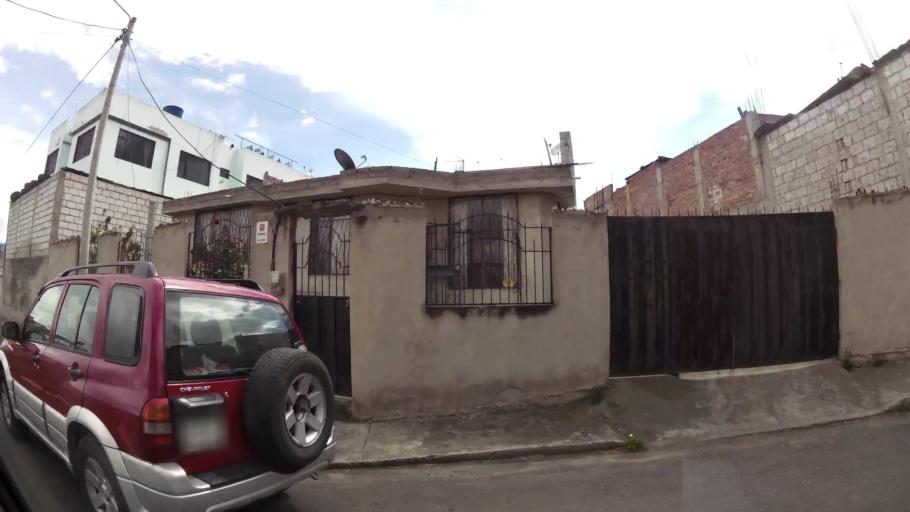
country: EC
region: Tungurahua
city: Ambato
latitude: -1.2580
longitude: -78.6184
